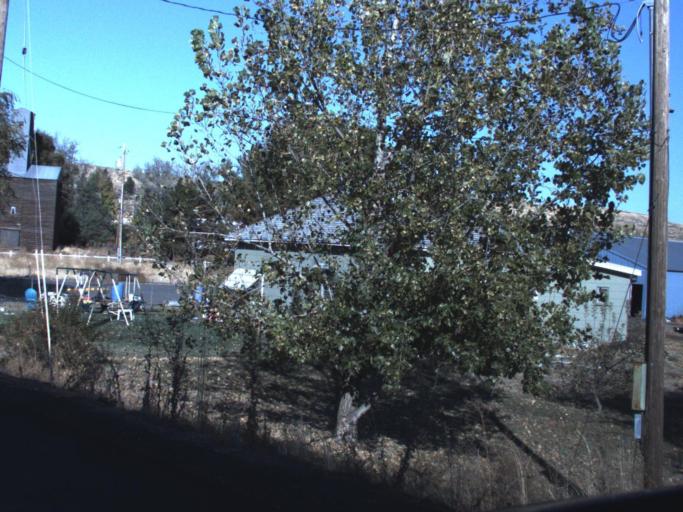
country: US
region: Washington
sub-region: Franklin County
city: Connell
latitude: 46.6414
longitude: -118.5524
